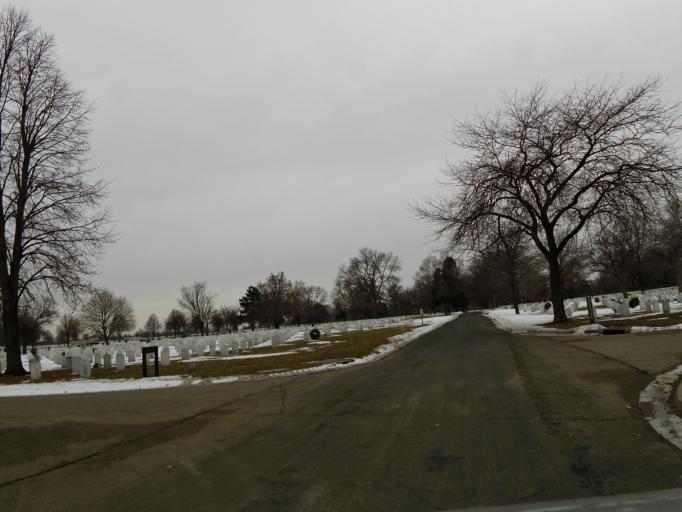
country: US
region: Minnesota
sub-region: Hennepin County
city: Richfield
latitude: 44.8735
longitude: -93.2141
